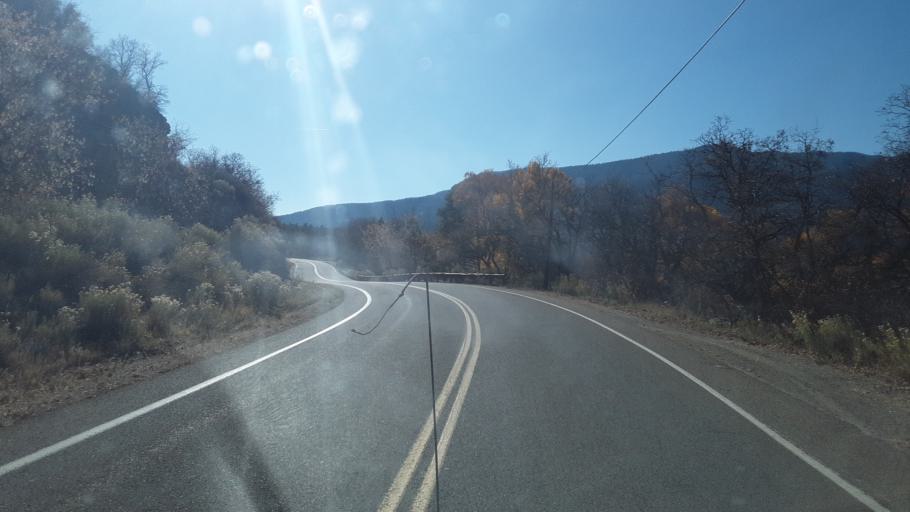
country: US
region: Colorado
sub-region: La Plata County
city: Durango
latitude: 37.3909
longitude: -107.8258
